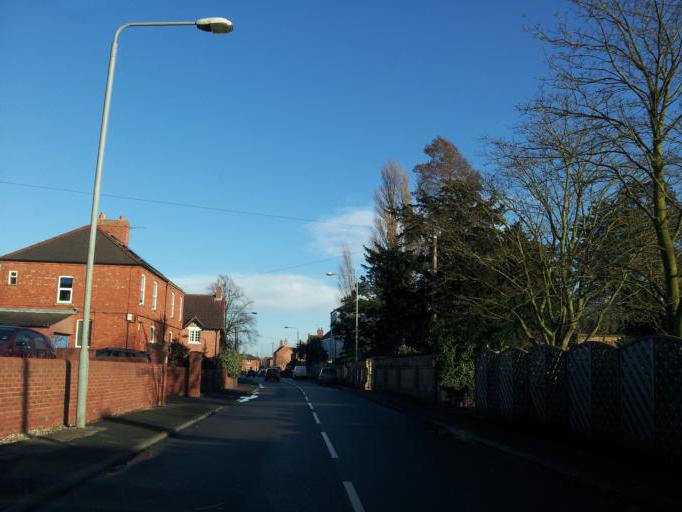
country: GB
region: England
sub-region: Nottinghamshire
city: Newark on Trent
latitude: 53.0555
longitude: -0.7747
